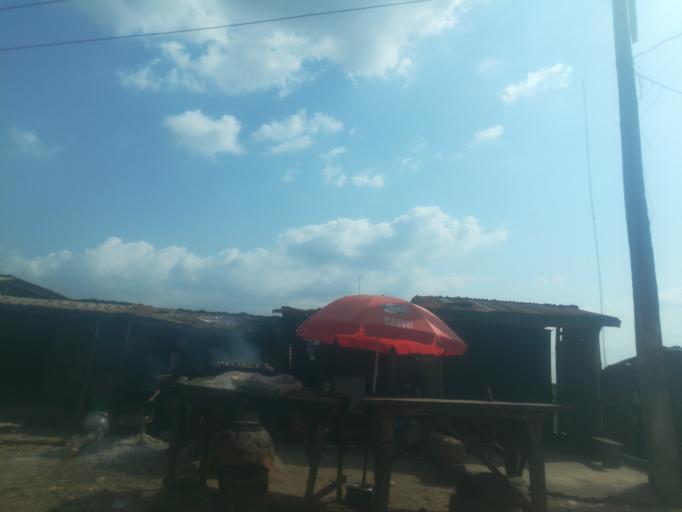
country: NG
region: Oyo
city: Moniya
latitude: 7.5251
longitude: 3.9110
